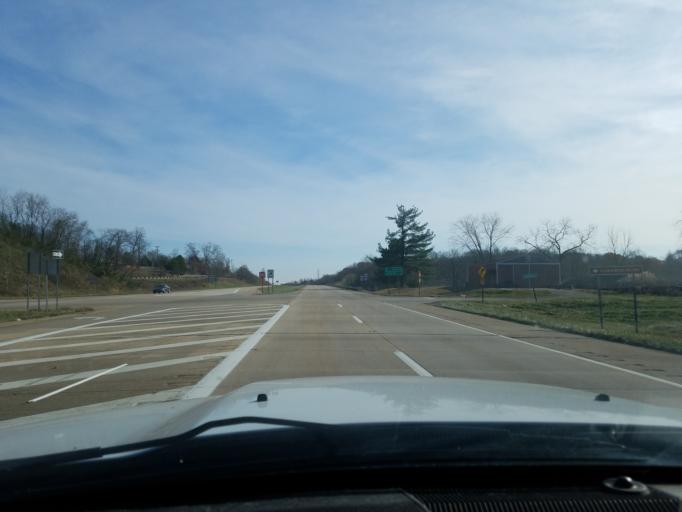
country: US
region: West Virginia
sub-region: Wood County
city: Washington
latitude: 39.2219
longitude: -81.8682
